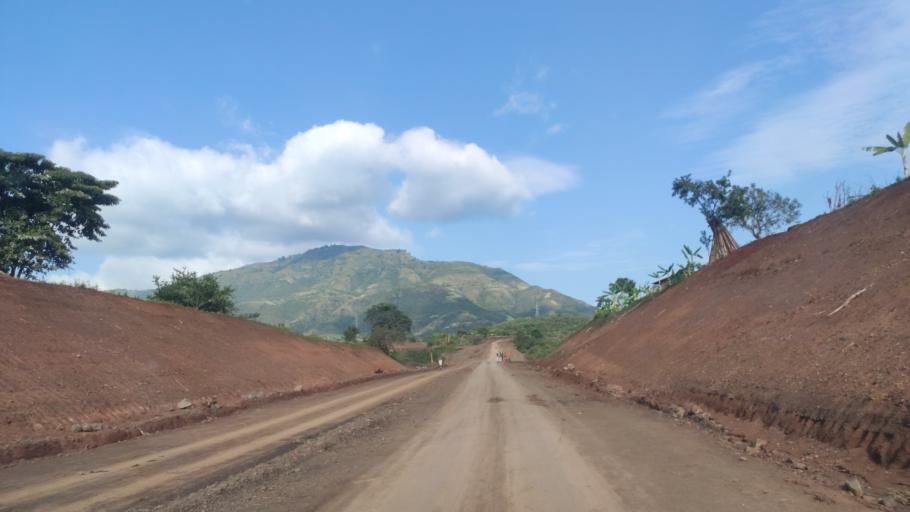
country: ET
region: Southern Nations, Nationalities, and People's Region
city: Arba Minch'
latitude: 6.4265
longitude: 37.3227
